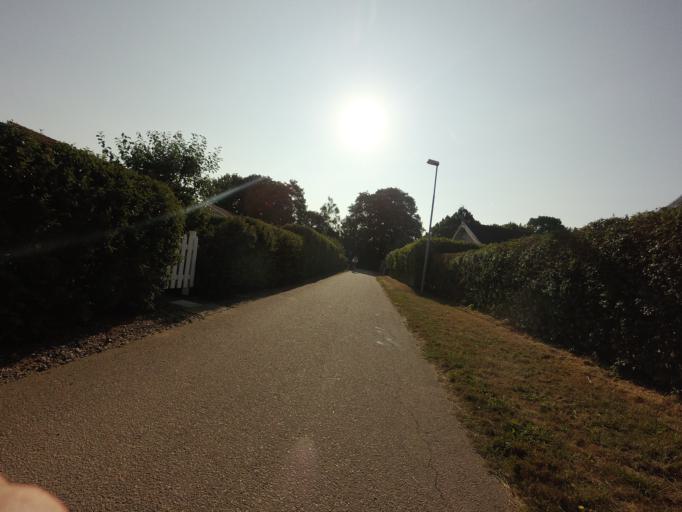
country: SE
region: Skane
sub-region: Landskrona
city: Asmundtorp
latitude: 55.8566
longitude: 12.9062
